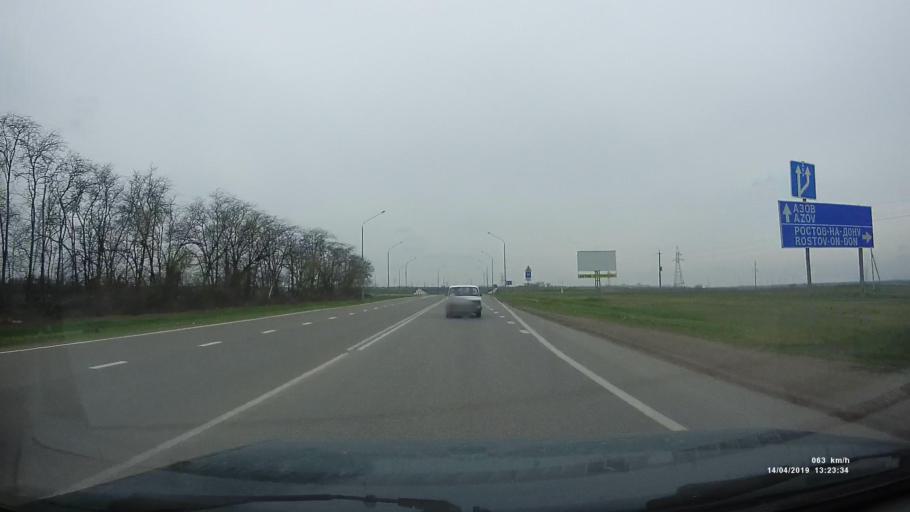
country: RU
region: Rostov
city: Kuleshovka
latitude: 47.0837
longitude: 39.4986
